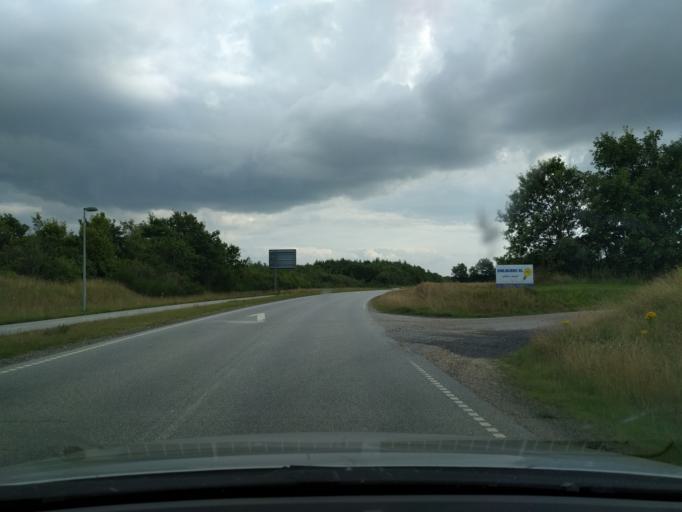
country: DK
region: Central Jutland
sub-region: Herning Kommune
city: Snejbjerg
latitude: 56.1167
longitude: 8.9073
